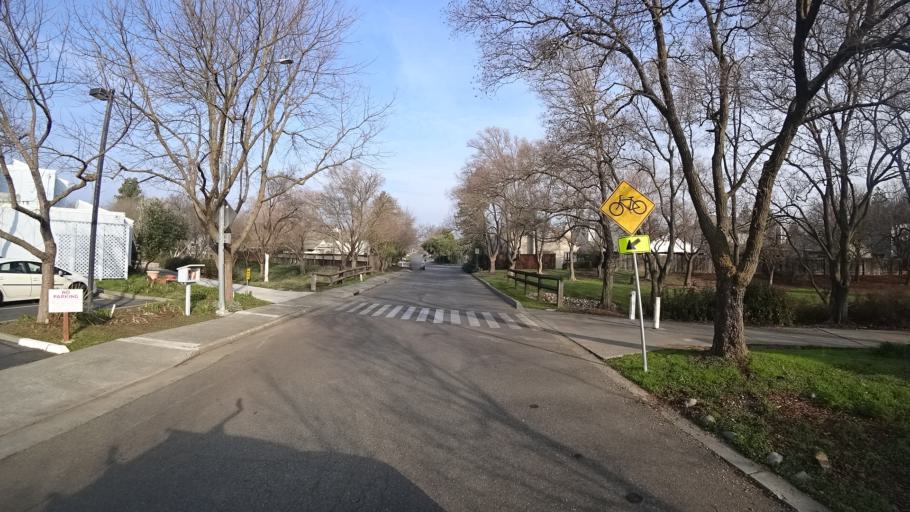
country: US
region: California
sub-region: Yolo County
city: Davis
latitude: 38.5654
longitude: -121.7642
